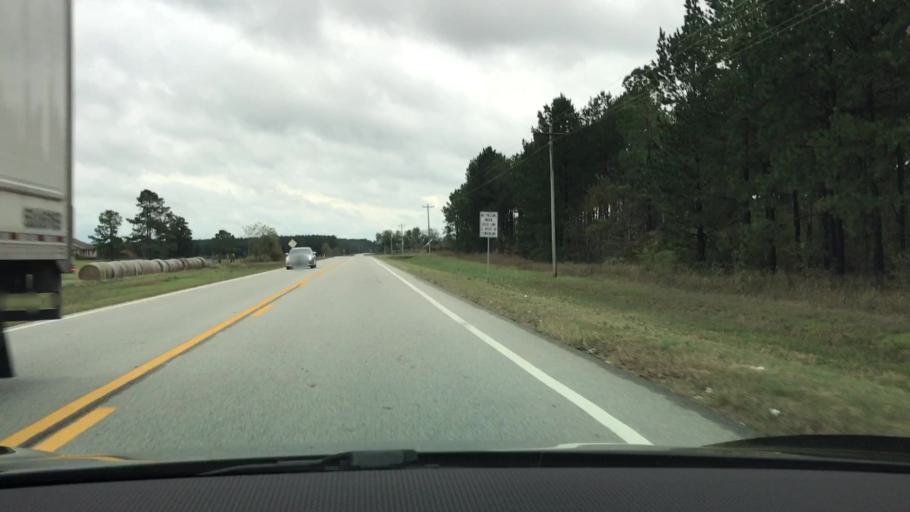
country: US
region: Georgia
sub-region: Glascock County
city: Gibson
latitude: 33.2944
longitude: -82.5122
